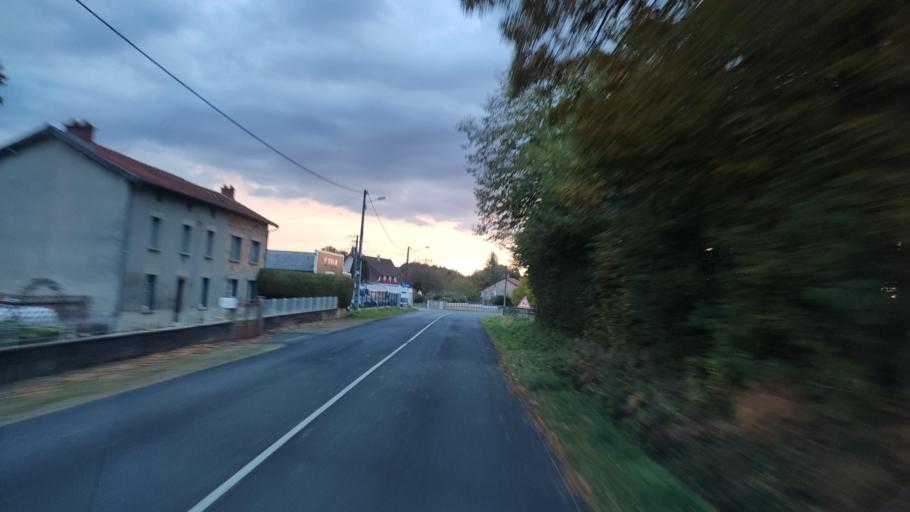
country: FR
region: Limousin
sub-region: Departement de la Haute-Vienne
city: Ambazac
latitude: 45.9387
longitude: 1.3590
